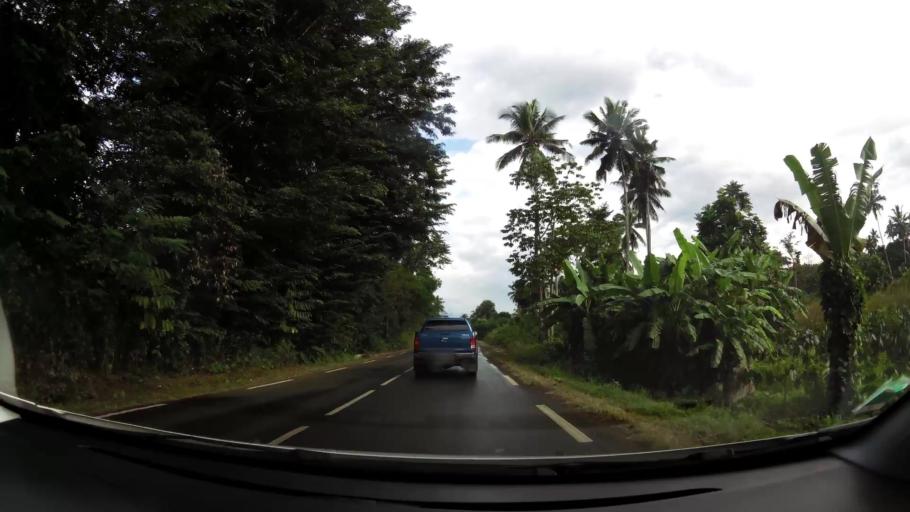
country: YT
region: Ouangani
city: Ouangani
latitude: -12.8354
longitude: 45.1423
